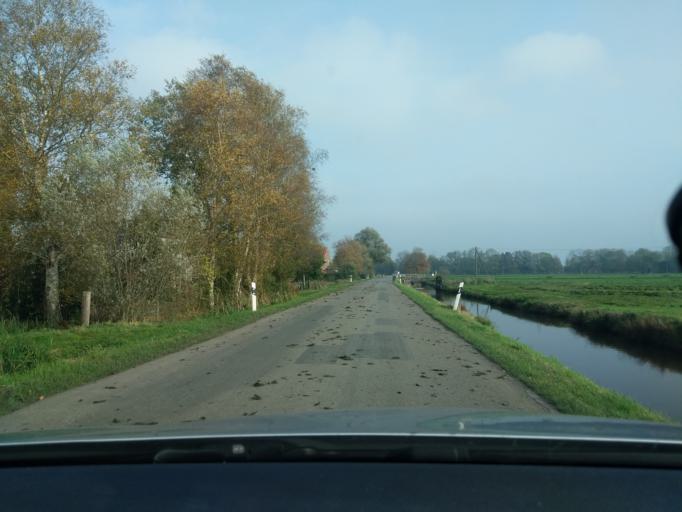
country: DE
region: Lower Saxony
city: Nordleda
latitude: 53.7273
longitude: 8.8394
